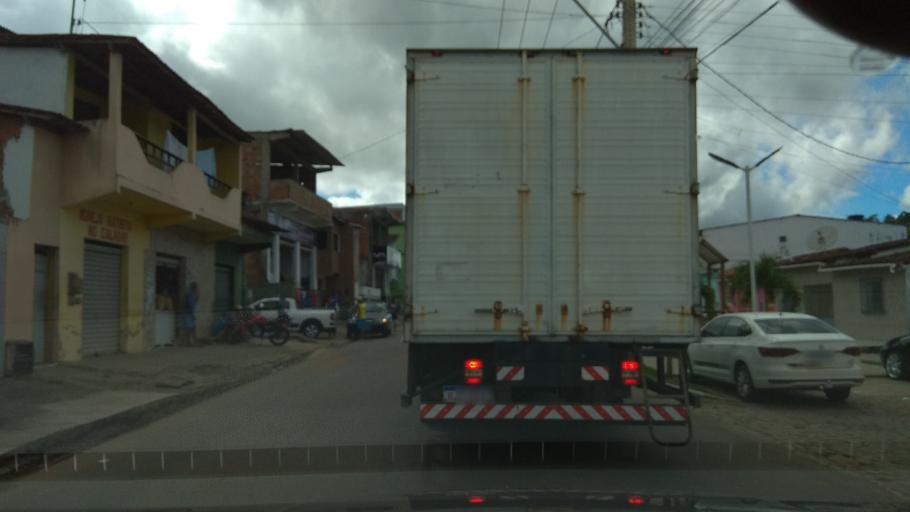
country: BR
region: Bahia
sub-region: Mutuipe
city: Mutuipe
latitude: -13.1778
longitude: -39.4123
